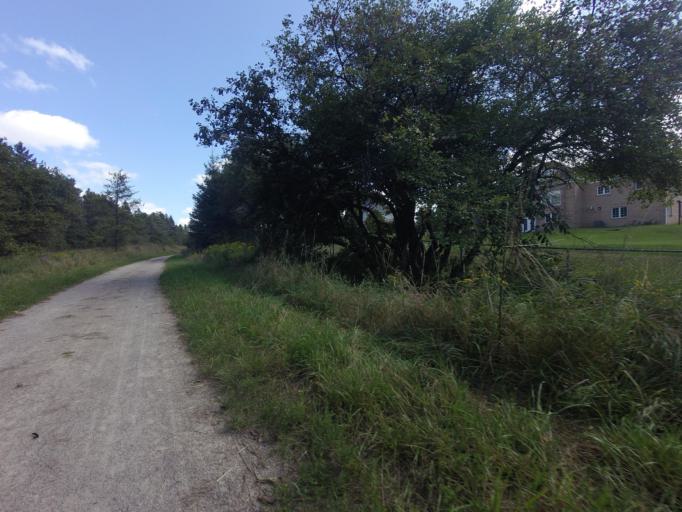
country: CA
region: Ontario
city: Orangeville
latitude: 43.7930
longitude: -80.3121
